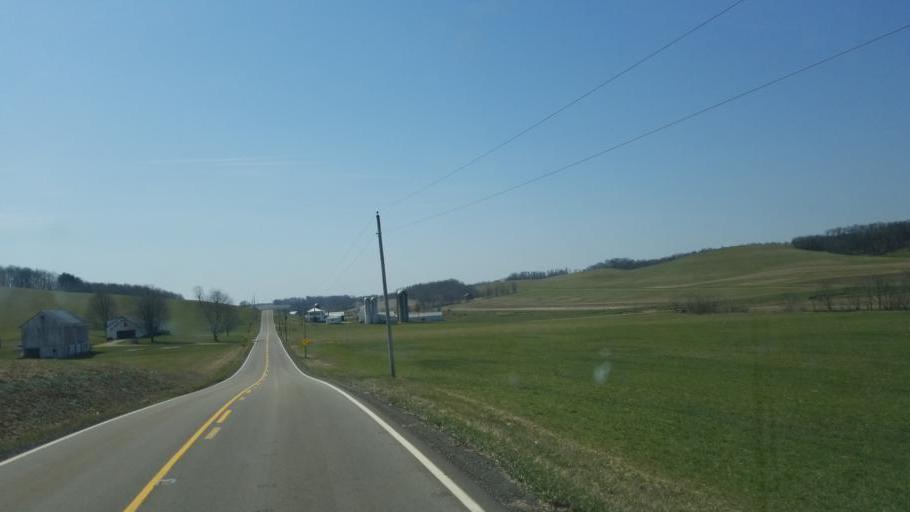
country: US
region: Ohio
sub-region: Knox County
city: Danville
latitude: 40.5315
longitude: -82.3001
